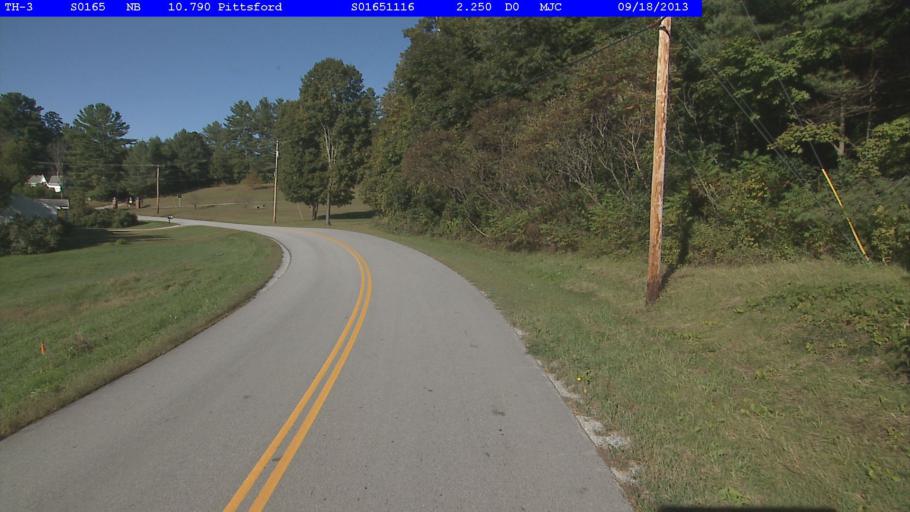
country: US
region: Vermont
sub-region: Rutland County
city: Rutland
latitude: 43.7136
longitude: -73.0132
